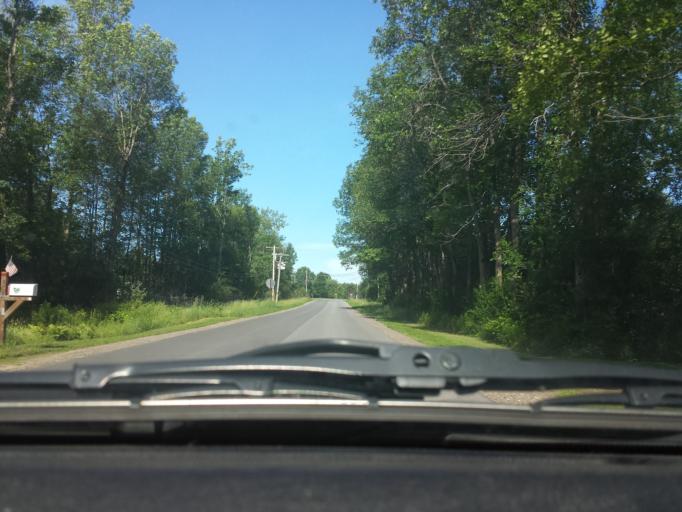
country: US
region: New York
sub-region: St. Lawrence County
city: Norwood
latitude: 44.7121
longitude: -74.9834
